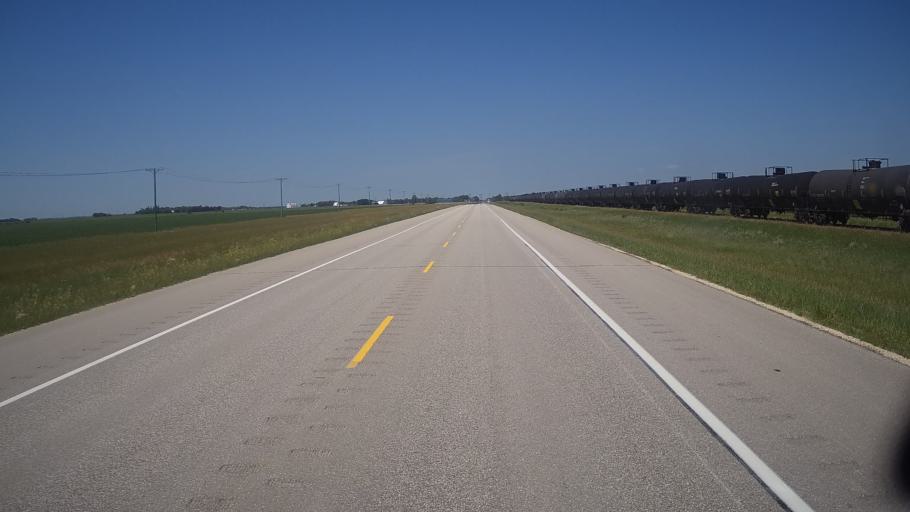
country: CA
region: Manitoba
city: Stonewall
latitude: 50.1146
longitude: -97.5193
